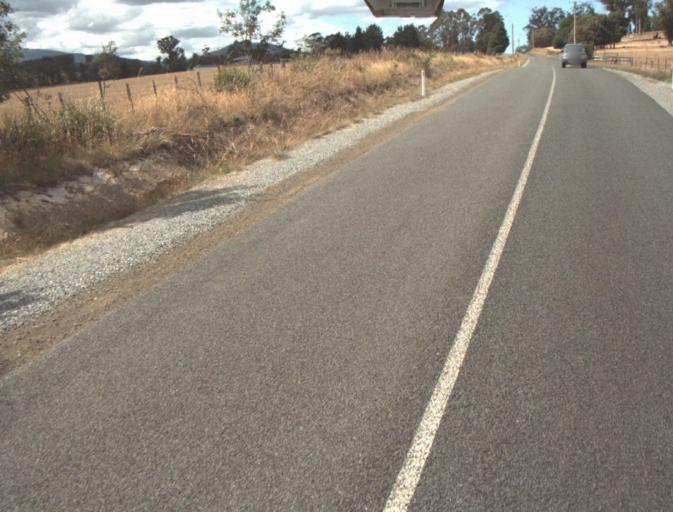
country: AU
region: Tasmania
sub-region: Launceston
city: Mayfield
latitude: -41.2120
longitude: 147.1340
